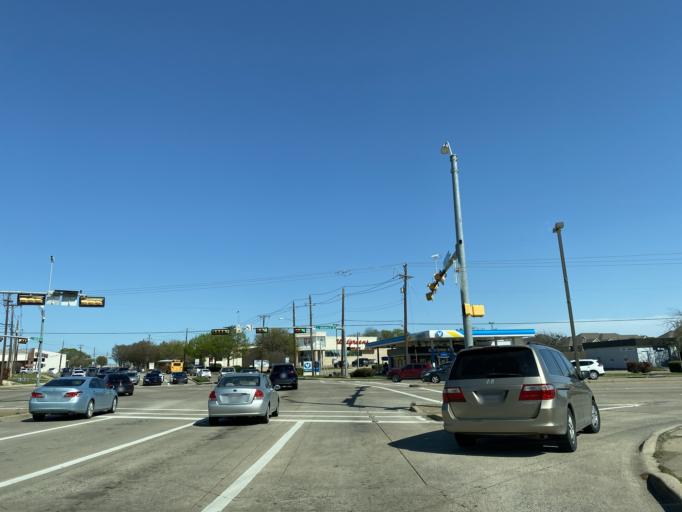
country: US
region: Texas
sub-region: Collin County
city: Allen
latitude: 33.1002
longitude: -96.6626
